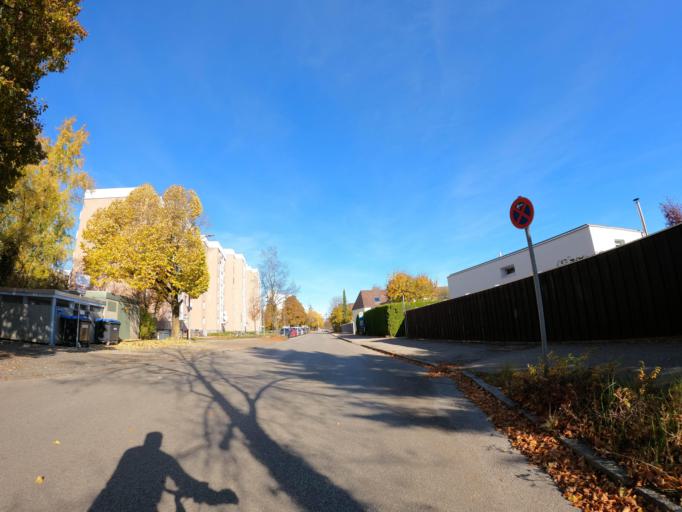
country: DE
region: Bavaria
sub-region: Upper Bavaria
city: Taufkirchen
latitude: 48.0482
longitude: 11.6043
